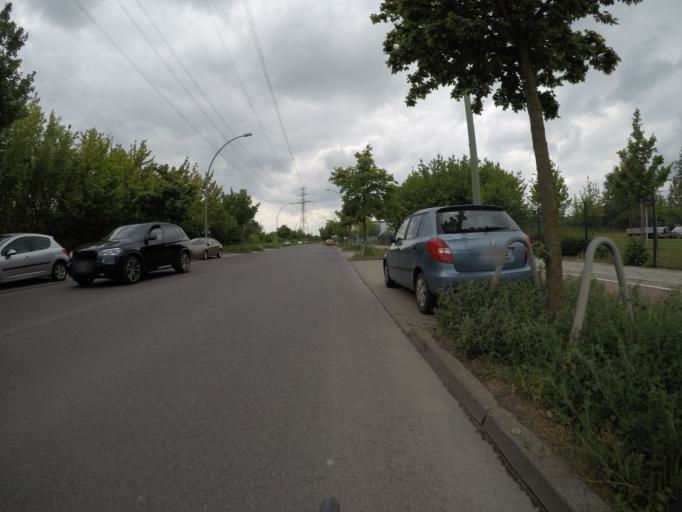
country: DE
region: Berlin
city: Falkenberg
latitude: 52.5533
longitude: 13.5380
